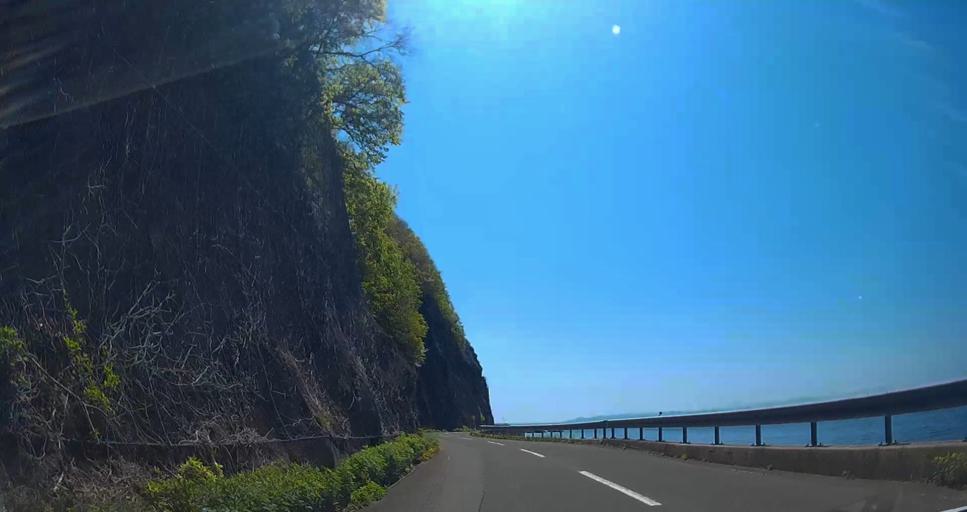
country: JP
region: Aomori
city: Aomori Shi
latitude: 41.1339
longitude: 140.7796
